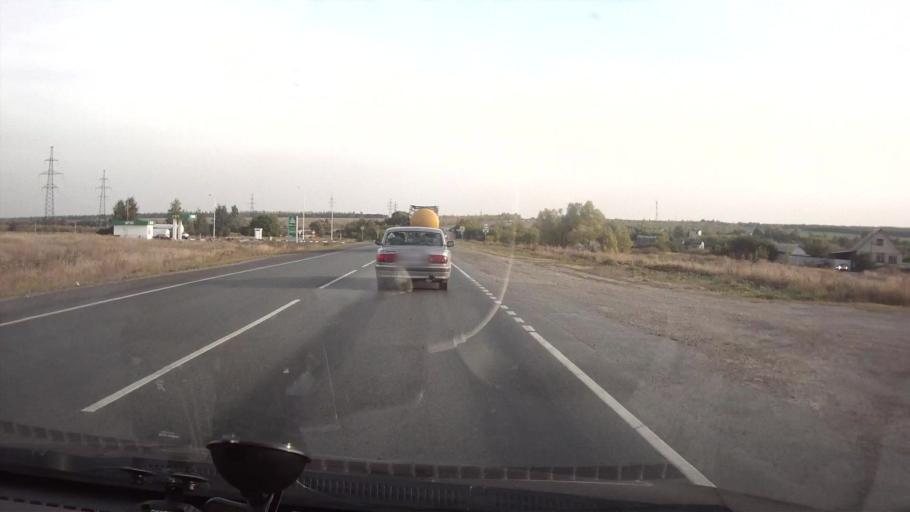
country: RU
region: Saratov
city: Sokolovyy
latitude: 51.5043
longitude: 45.8130
